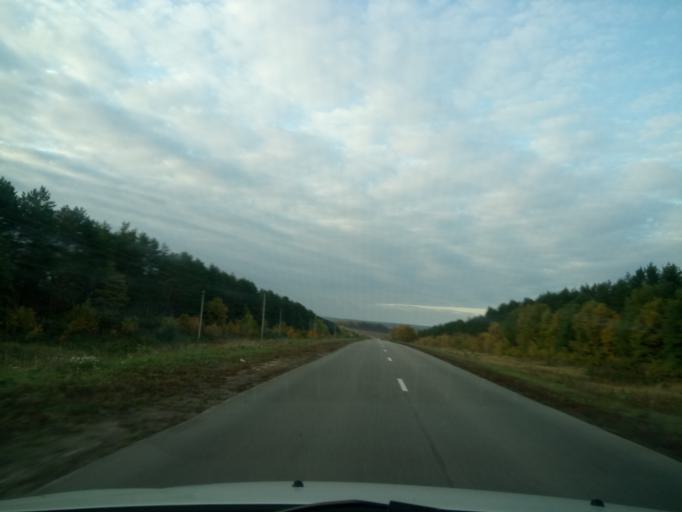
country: RU
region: Nizjnij Novgorod
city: Buturlino
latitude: 55.5271
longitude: 44.9933
